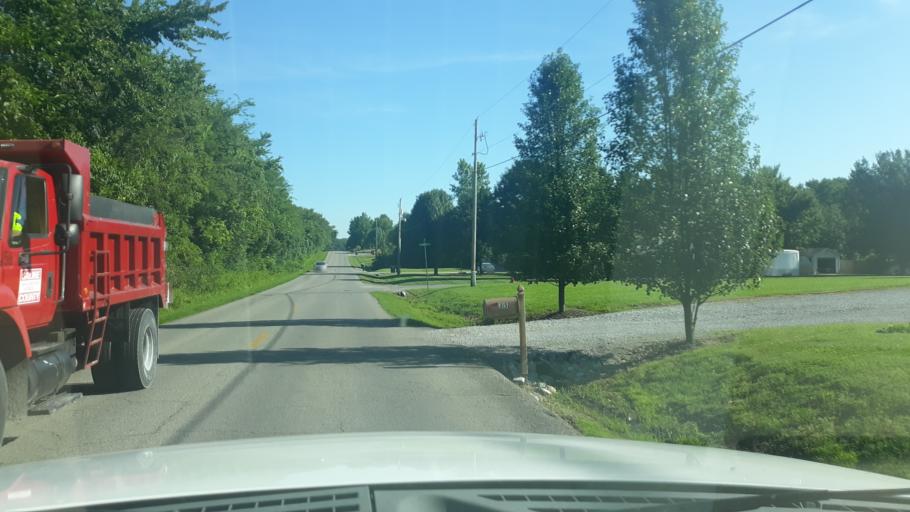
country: US
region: Illinois
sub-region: Saline County
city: Harrisburg
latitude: 37.7283
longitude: -88.5688
